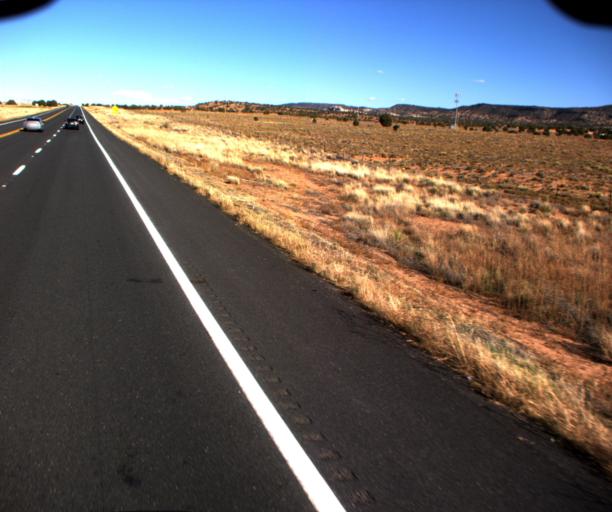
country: US
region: Arizona
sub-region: Coconino County
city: Kaibito
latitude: 36.4021
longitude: -110.8510
